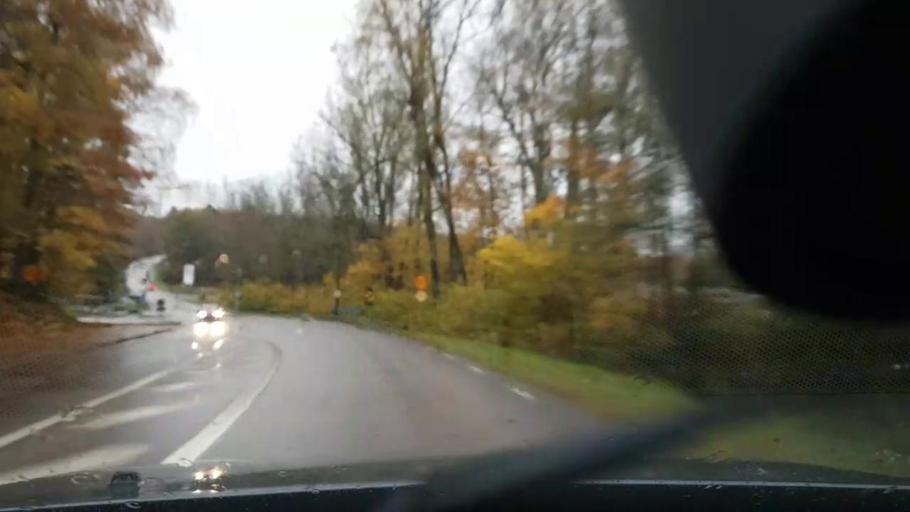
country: SE
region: Vaestra Goetaland
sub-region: Molndal
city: Lindome
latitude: 57.5971
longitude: 12.0839
